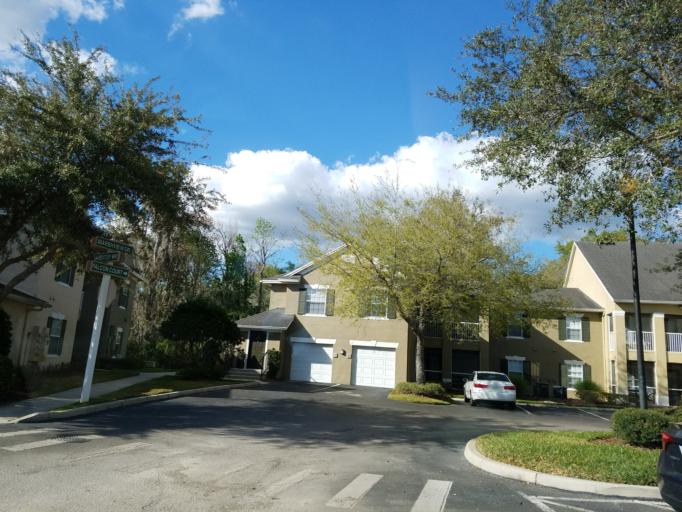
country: US
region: Florida
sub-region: Hillsborough County
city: Pebble Creek
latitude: 28.1906
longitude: -82.3689
